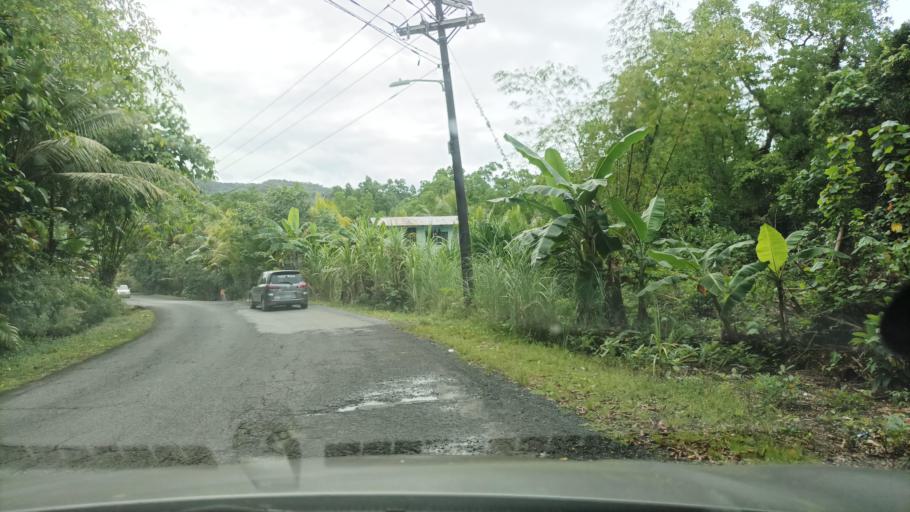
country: FM
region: Pohnpei
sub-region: Kolonia Municipality
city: Kolonia
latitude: 6.9400
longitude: 158.2778
